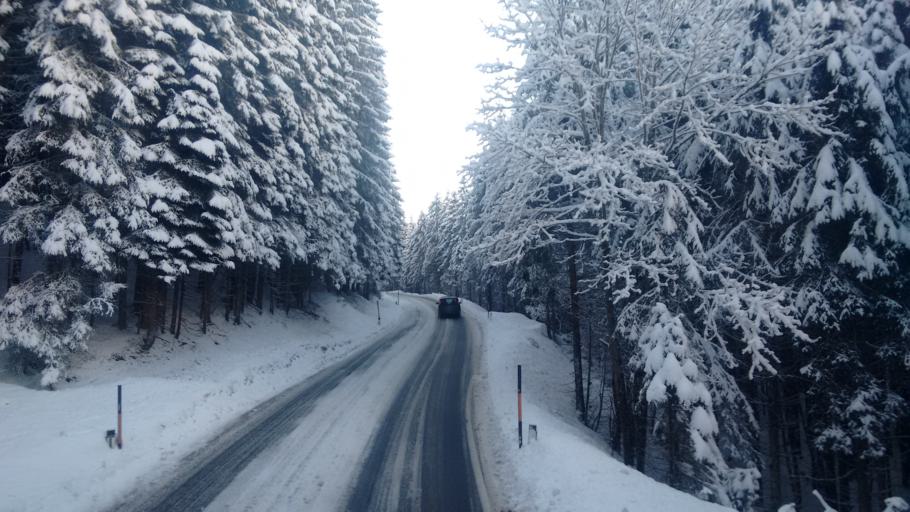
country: AT
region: Salzburg
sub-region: Politischer Bezirk Sankt Johann im Pongau
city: Untertauern
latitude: 47.3222
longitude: 13.4460
